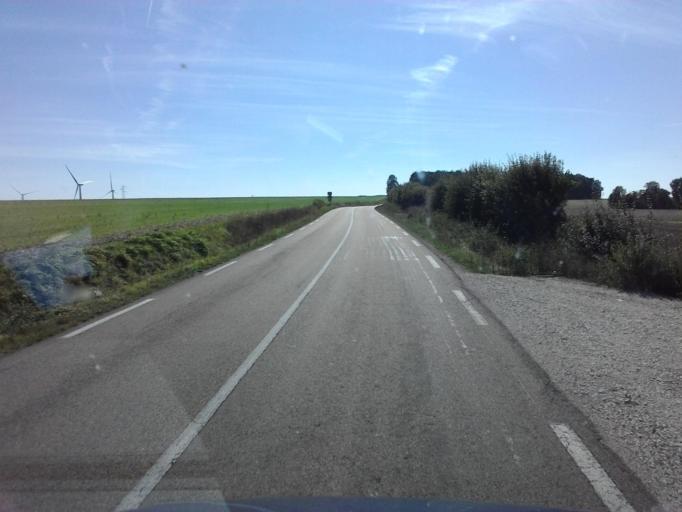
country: FR
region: Bourgogne
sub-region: Departement de l'Yonne
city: Tonnerre
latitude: 47.7888
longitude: 3.9470
